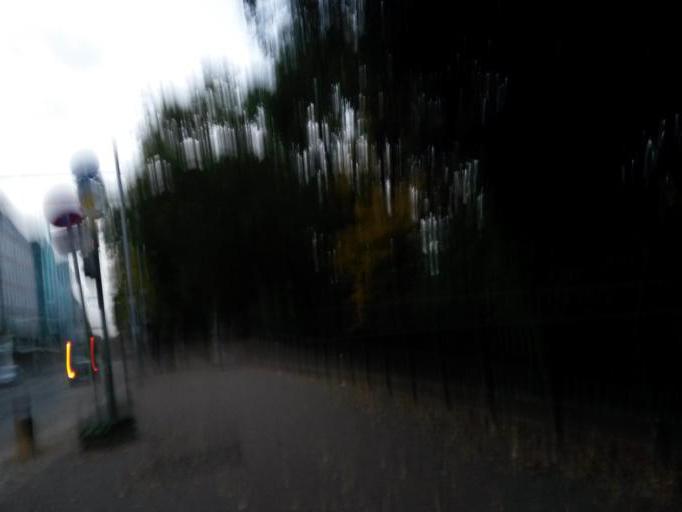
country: DE
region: Bremen
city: Bremen
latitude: 53.0770
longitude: 8.8118
